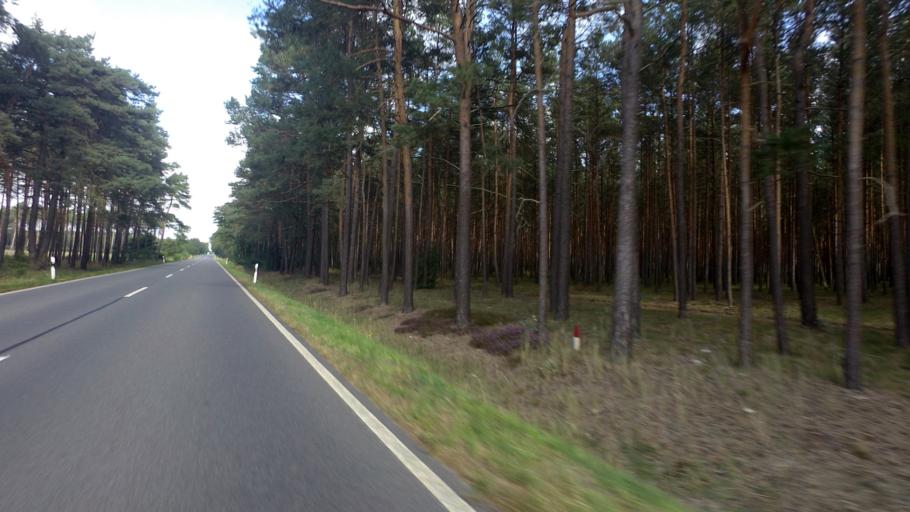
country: DE
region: Saxony-Anhalt
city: Holzdorf
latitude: 51.8679
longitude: 13.1453
